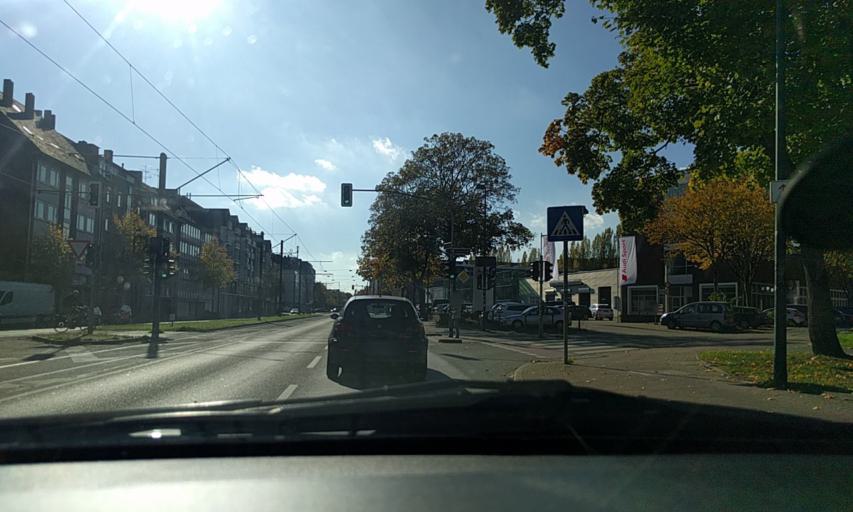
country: DE
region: North Rhine-Westphalia
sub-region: Regierungsbezirk Dusseldorf
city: Dusseldorf
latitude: 51.2127
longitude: 6.7979
